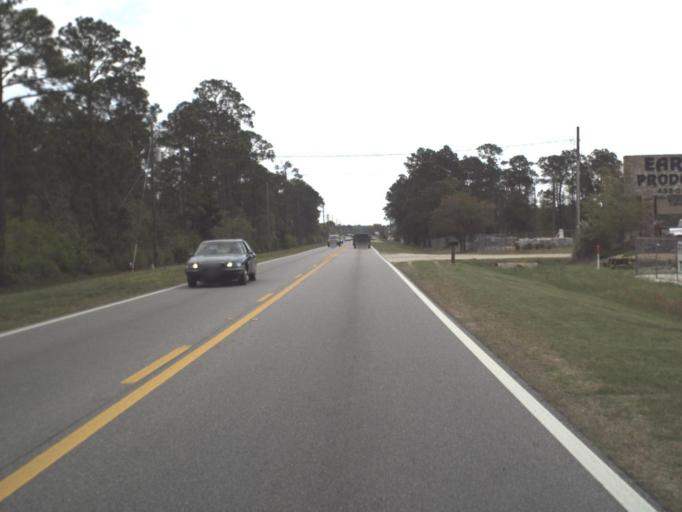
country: US
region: Florida
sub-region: Escambia County
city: Myrtle Grove
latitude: 30.3575
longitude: -87.3664
